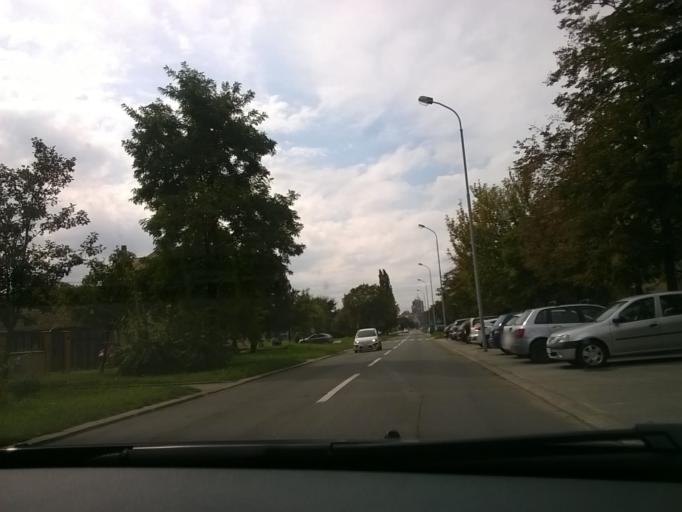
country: RS
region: Autonomna Pokrajina Vojvodina
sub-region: Juznobanatski Okrug
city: Pancevo
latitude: 44.8788
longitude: 20.6534
